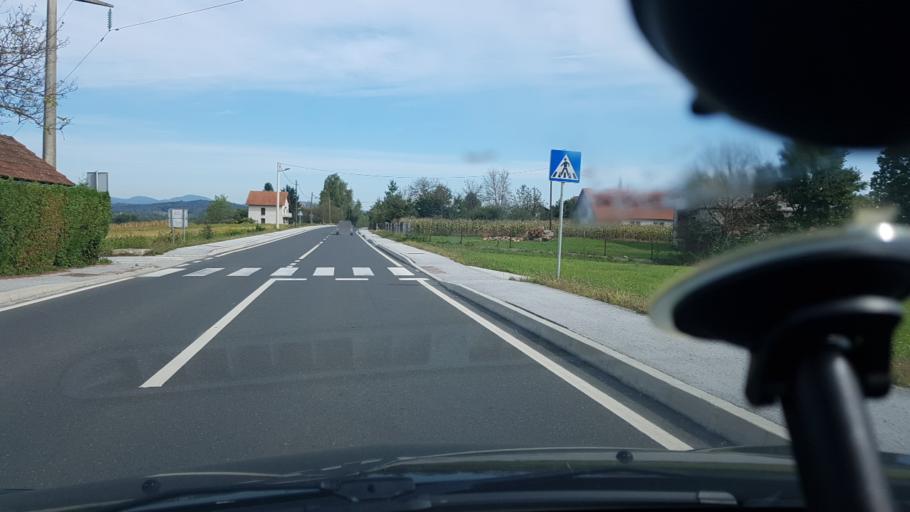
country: HR
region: Krapinsko-Zagorska
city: Marija Bistrica
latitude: 46.0633
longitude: 16.1867
